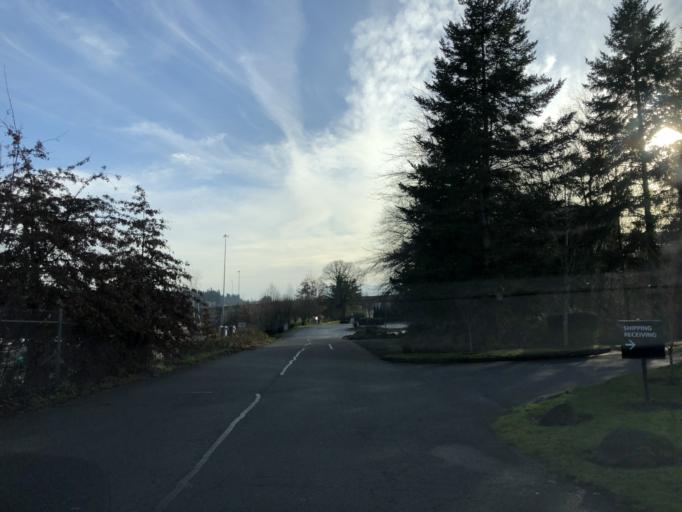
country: US
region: Oregon
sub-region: Washington County
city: Durham
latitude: 45.4238
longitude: -122.7448
